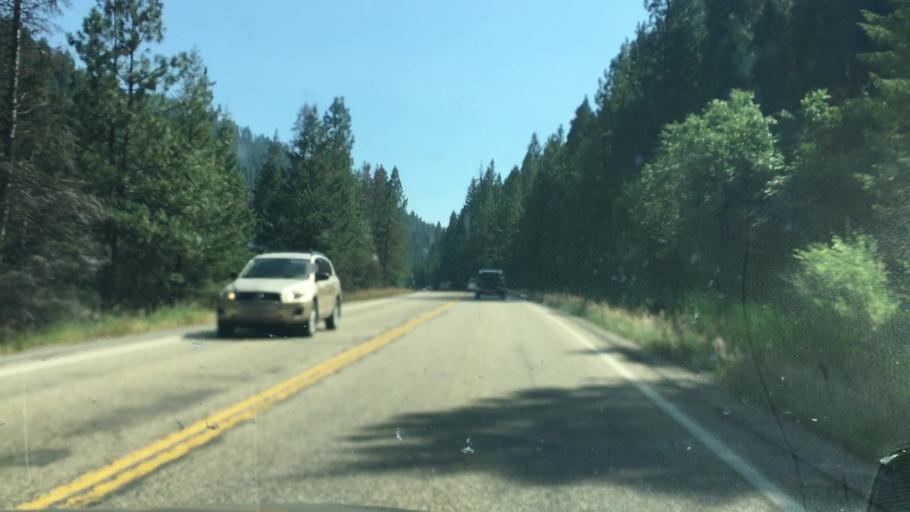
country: US
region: Idaho
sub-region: Valley County
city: Cascade
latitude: 44.2359
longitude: -116.1038
